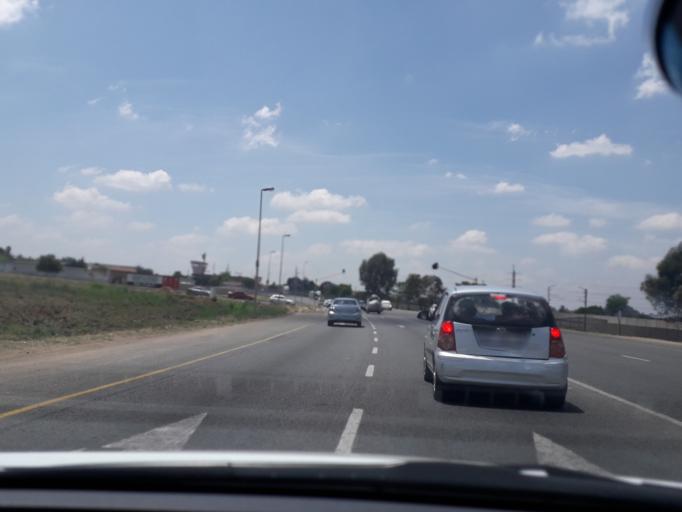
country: ZA
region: Gauteng
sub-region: City of Johannesburg Metropolitan Municipality
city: Midrand
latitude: -26.0064
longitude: 28.1360
